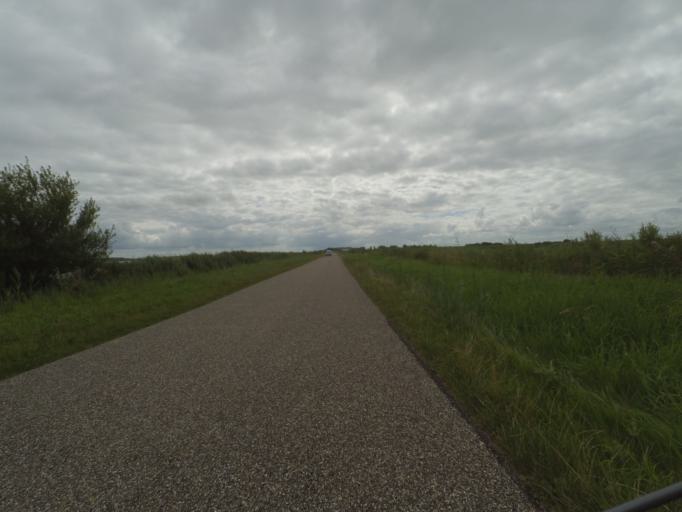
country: NL
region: Friesland
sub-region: Gemeente Dongeradeel
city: Anjum
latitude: 53.3484
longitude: 6.1530
